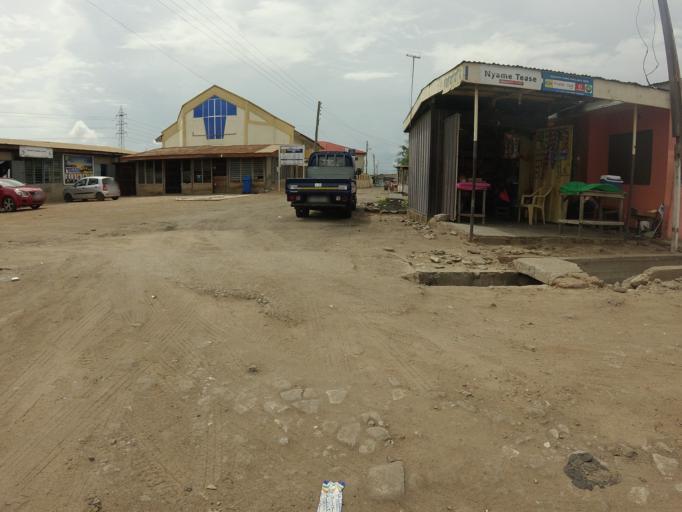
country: GH
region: Greater Accra
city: Accra
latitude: 5.5974
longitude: -0.2196
